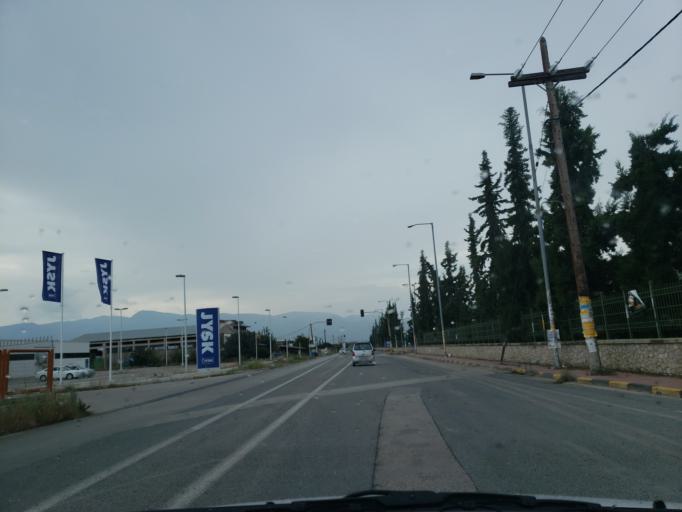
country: GR
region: Central Greece
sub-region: Nomos Fthiotidos
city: Lamia
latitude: 38.8757
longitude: 22.4393
